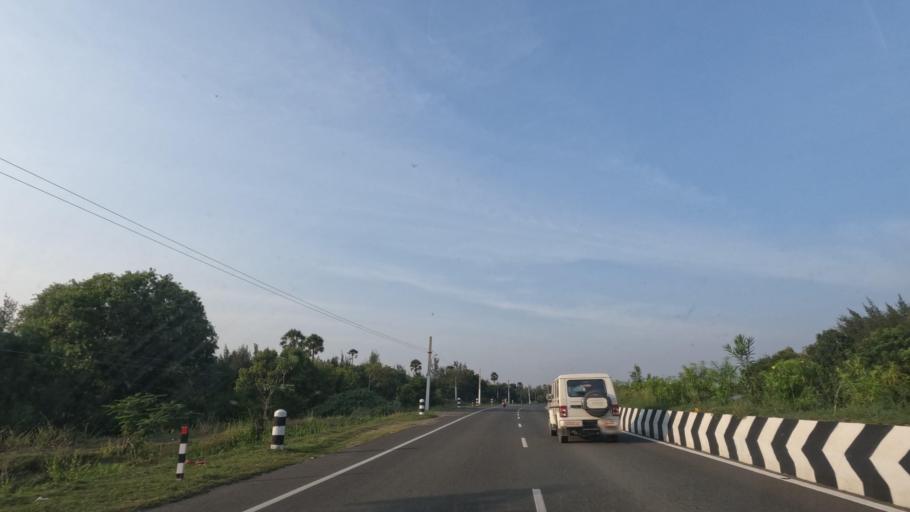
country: IN
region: Tamil Nadu
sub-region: Kancheepuram
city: Mamallapuram
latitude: 12.6666
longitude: 80.2097
